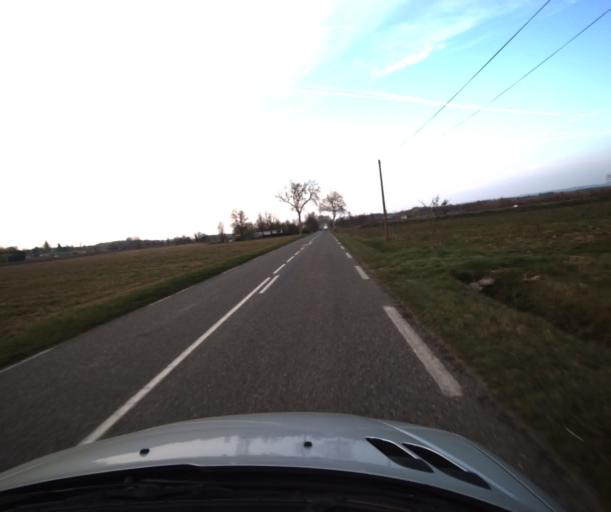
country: FR
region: Midi-Pyrenees
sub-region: Departement de la Haute-Garonne
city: Fronton
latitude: 43.8679
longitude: 1.3811
